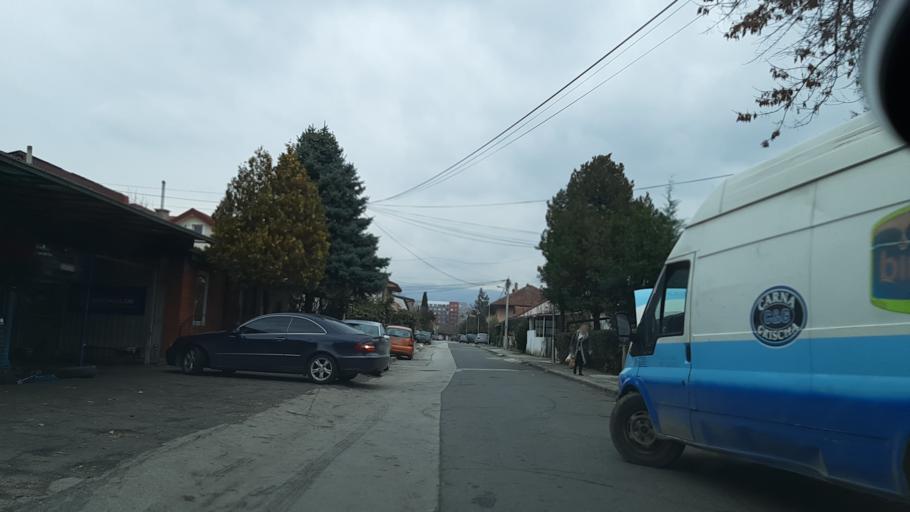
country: MK
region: Kisela Voda
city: Usje
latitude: 41.9760
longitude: 21.4676
